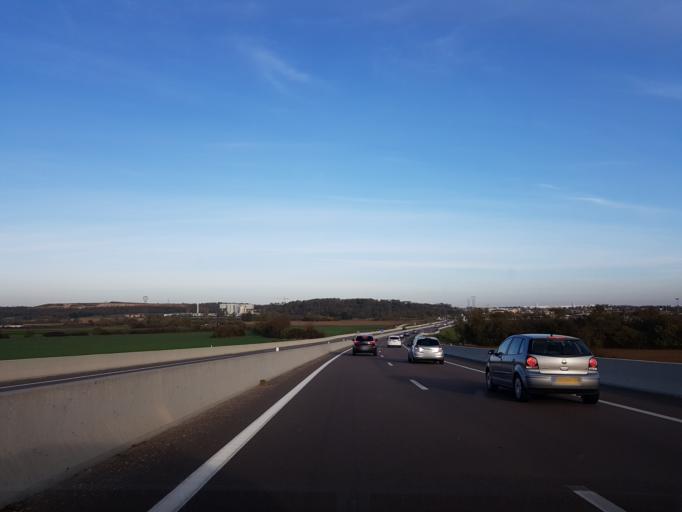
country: FR
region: Bourgogne
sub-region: Departement de la Cote-d'Or
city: Ahuy
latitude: 47.3579
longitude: 5.0231
